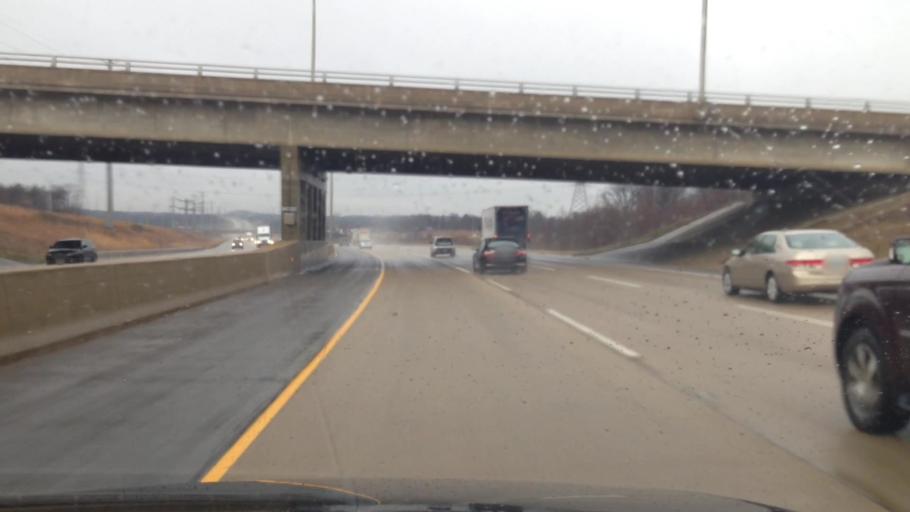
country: US
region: Illinois
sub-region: Cook County
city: Lemont
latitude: 41.6268
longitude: -88.0107
